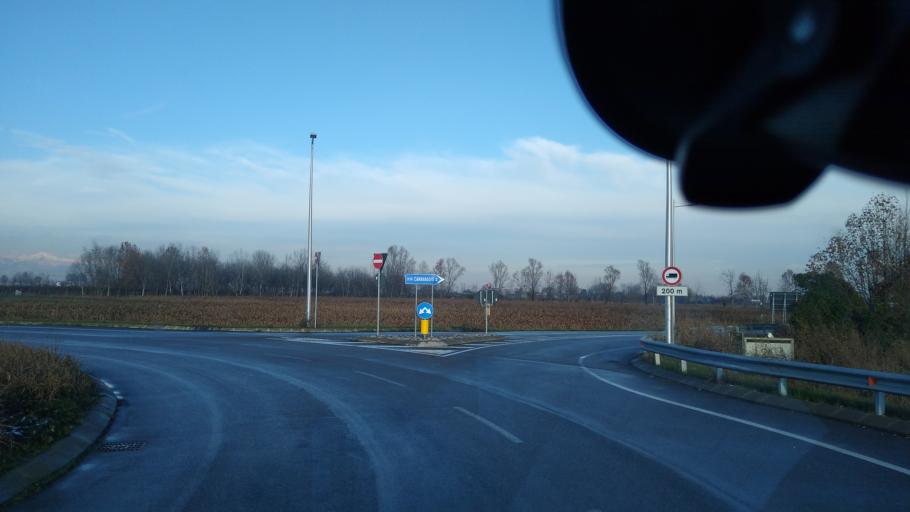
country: IT
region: Lombardy
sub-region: Provincia di Bergamo
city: Calvenzano
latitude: 45.4945
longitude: 9.6166
